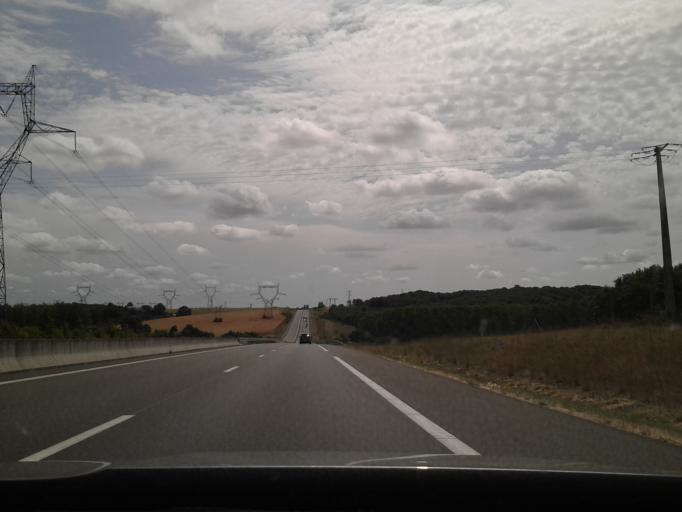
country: FR
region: Centre
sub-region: Departement d'Indre-et-Loire
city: Cerelles
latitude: 47.4890
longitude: 0.6691
